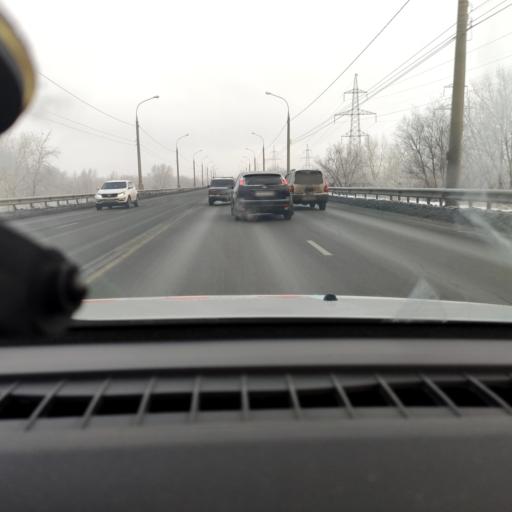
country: RU
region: Samara
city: Samara
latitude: 53.1567
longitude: 50.1917
